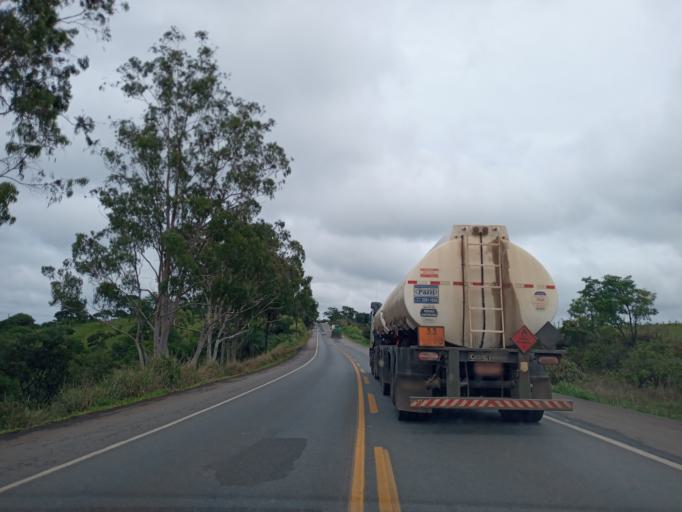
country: BR
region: Minas Gerais
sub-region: Campos Altos
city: Campos Altos
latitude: -19.5966
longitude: -46.2947
